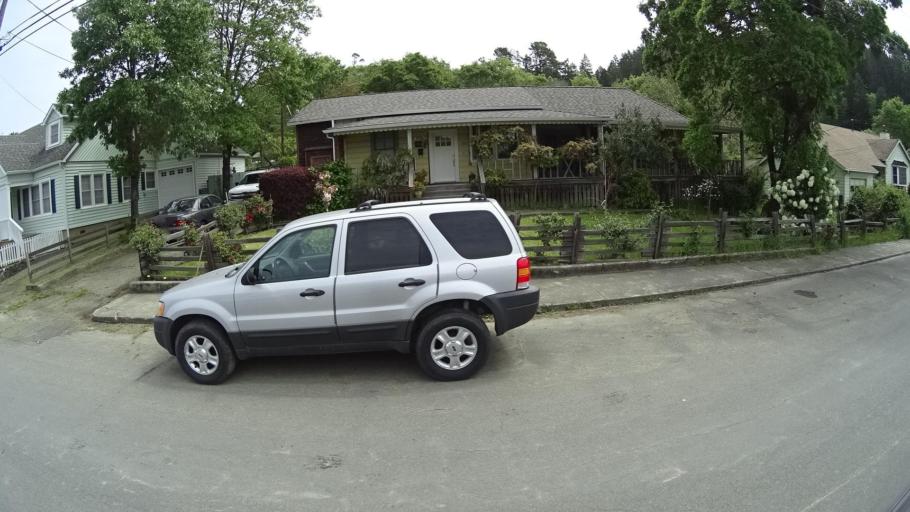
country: US
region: California
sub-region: Humboldt County
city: Redway
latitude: 40.0994
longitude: -123.7937
